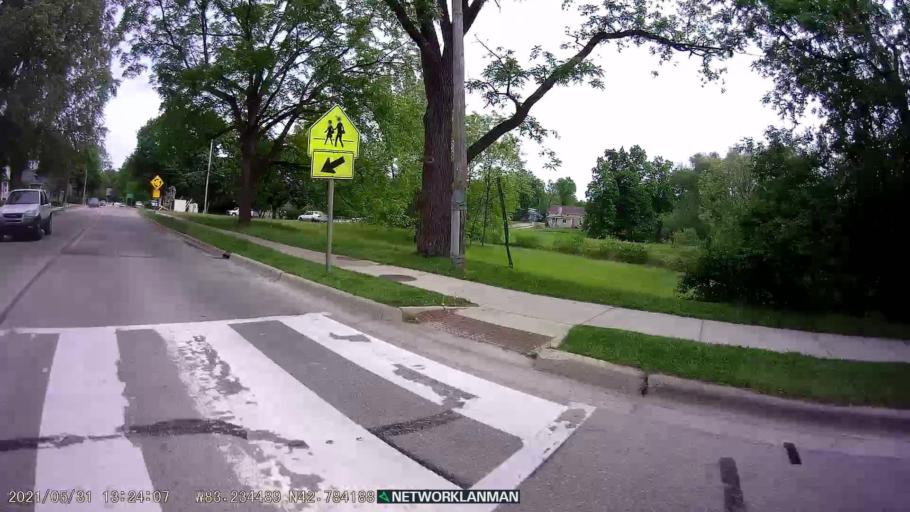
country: US
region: Michigan
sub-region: Oakland County
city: Lake Orion
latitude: 42.7841
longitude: -83.2344
